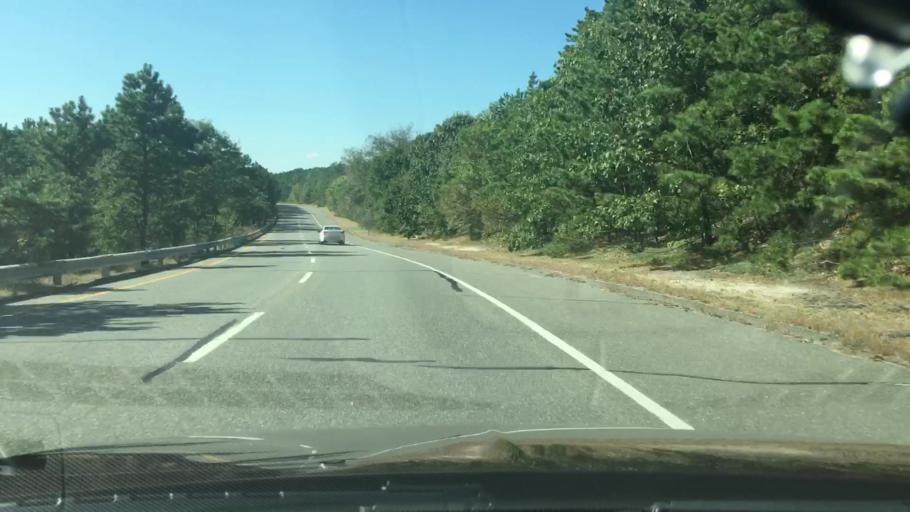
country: US
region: New York
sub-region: Suffolk County
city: North Patchogue
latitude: 40.7953
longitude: -73.0271
